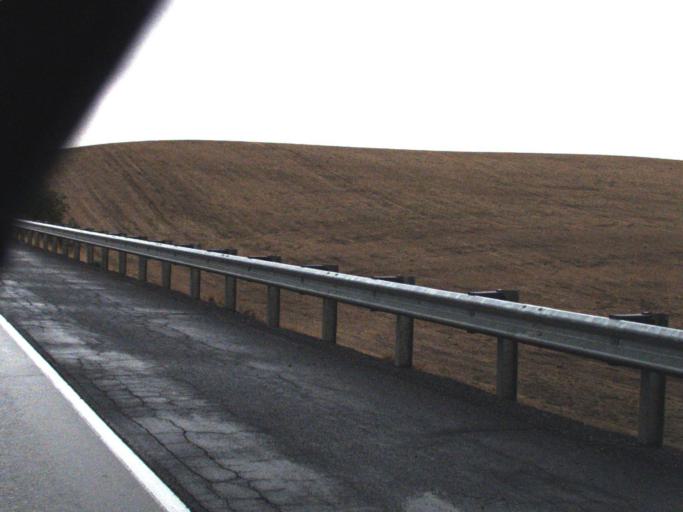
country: US
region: Washington
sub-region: Whitman County
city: Colfax
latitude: 47.1725
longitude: -117.3802
